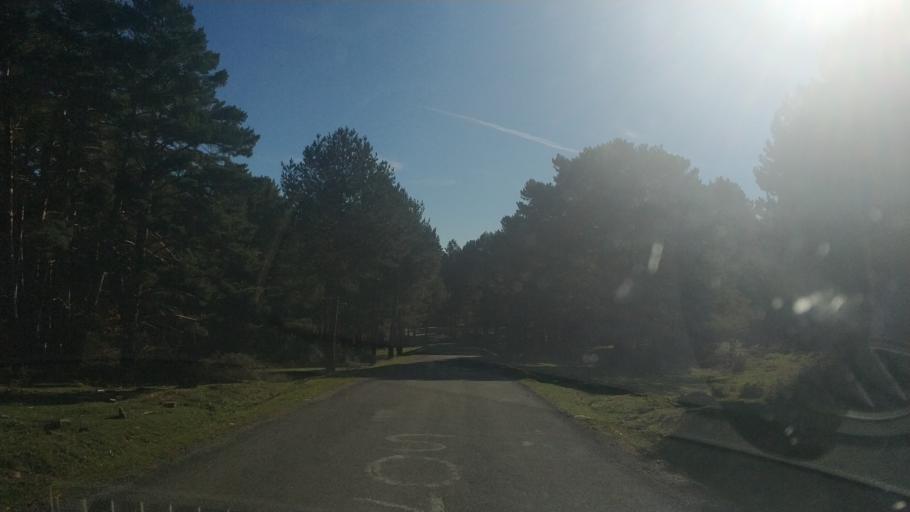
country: ES
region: Castille and Leon
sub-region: Provincia de Soria
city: Vinuesa
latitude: 41.9640
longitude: -2.7893
